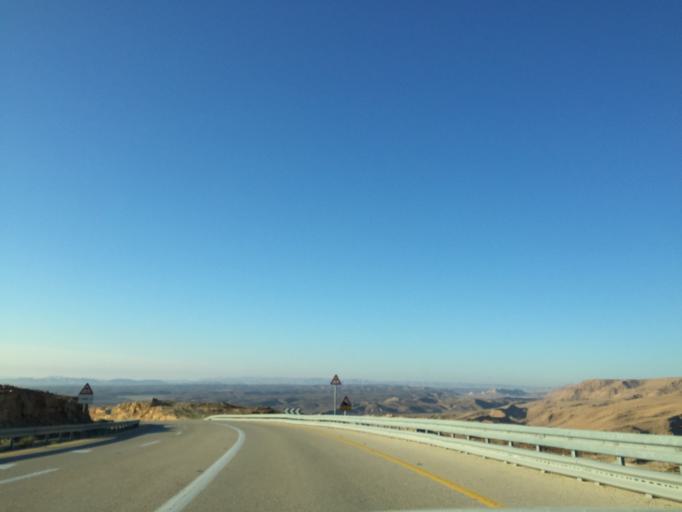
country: IL
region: Southern District
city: Mitzpe Ramon
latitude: 30.4997
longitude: 34.9378
